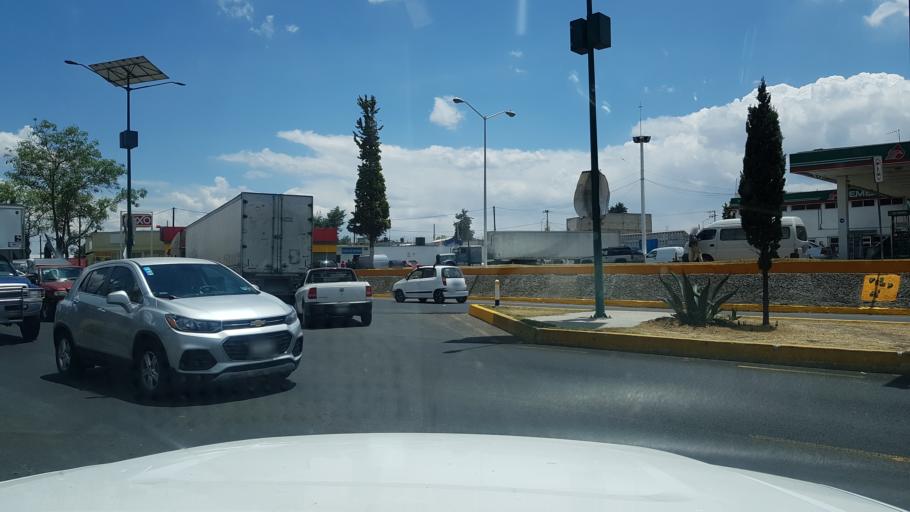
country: MX
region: Hidalgo
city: Calpulalpan
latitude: 19.5928
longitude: -98.5766
